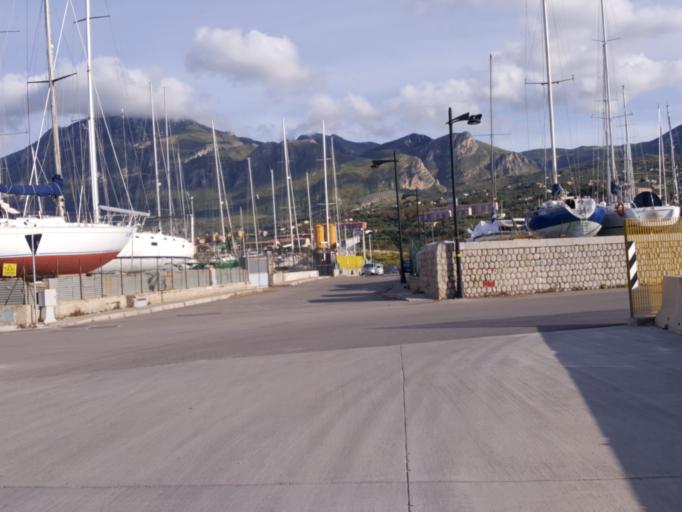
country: IT
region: Sicily
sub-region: Palermo
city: Termini Imerese
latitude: 37.9852
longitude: 13.7049
